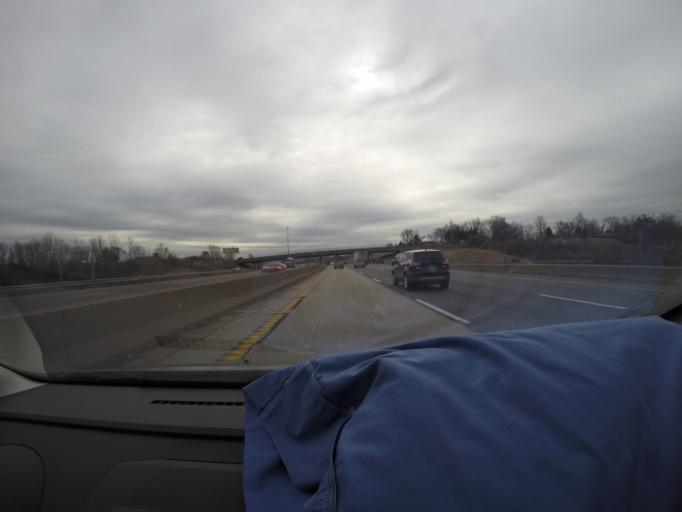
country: US
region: Missouri
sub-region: Saint Louis County
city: Bridgeton
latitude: 38.7472
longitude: -90.4360
